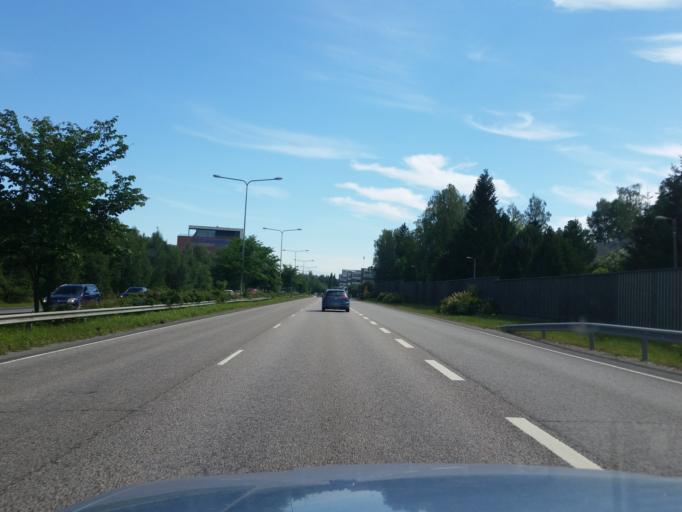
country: FI
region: Uusimaa
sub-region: Helsinki
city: Otaniemi
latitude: 60.1918
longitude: 24.8067
